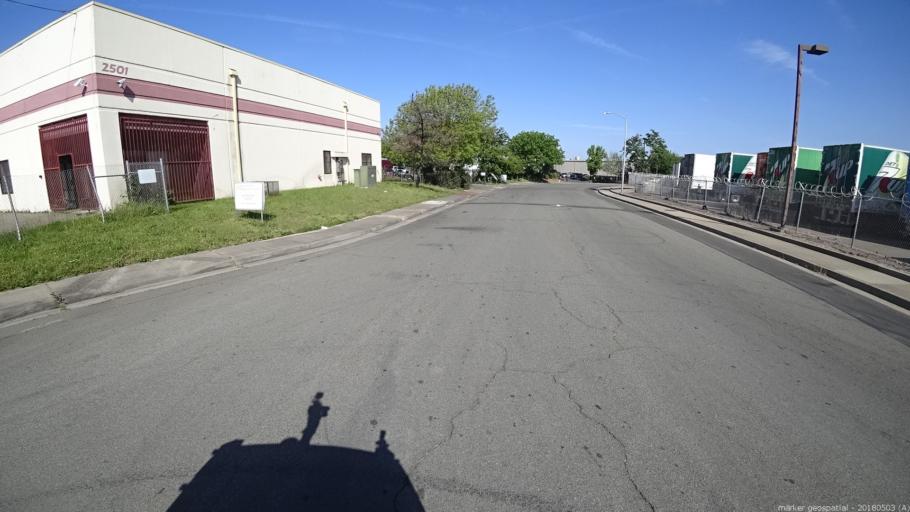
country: US
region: California
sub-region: Sacramento County
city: Arden-Arcade
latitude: 38.6141
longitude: -121.4340
